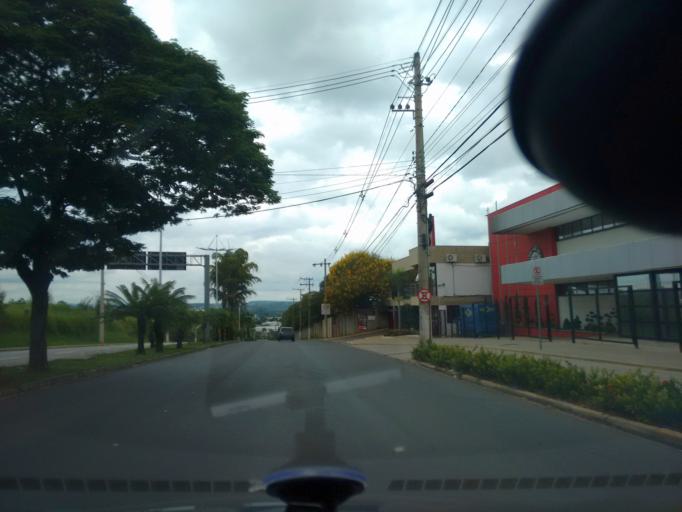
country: BR
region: Sao Paulo
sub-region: Indaiatuba
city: Indaiatuba
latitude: -23.0849
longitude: -47.1929
